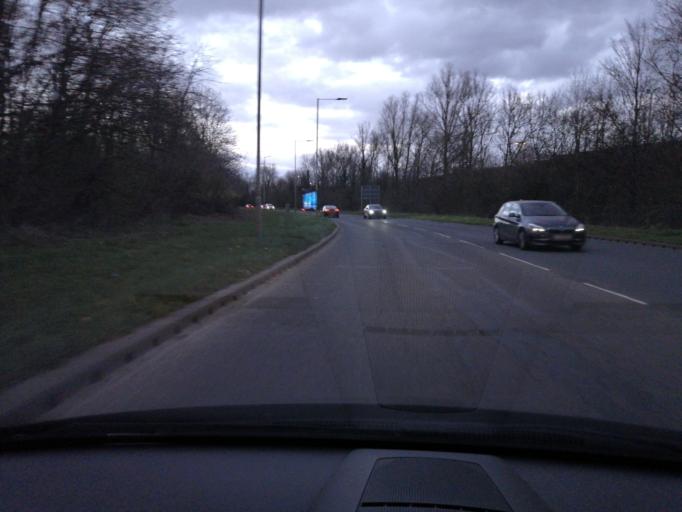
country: GB
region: England
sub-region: Peterborough
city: Eye
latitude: 52.5933
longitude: -0.2041
